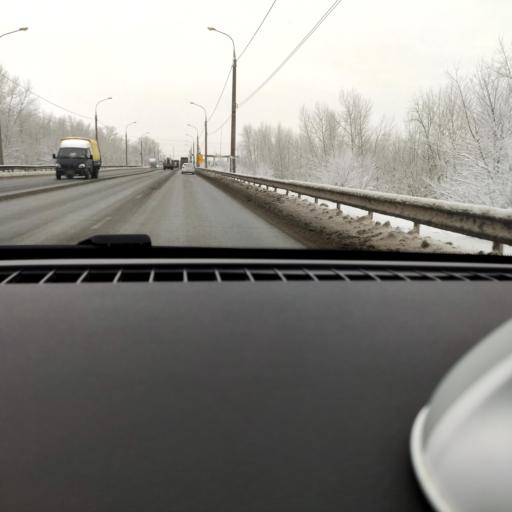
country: RU
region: Samara
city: Samara
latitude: 53.1477
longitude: 50.1827
